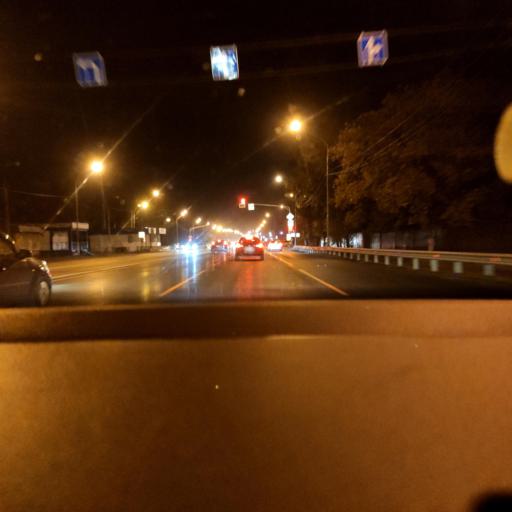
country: RU
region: Moskovskaya
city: Naro-Fominsk
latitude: 55.3648
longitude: 36.7571
